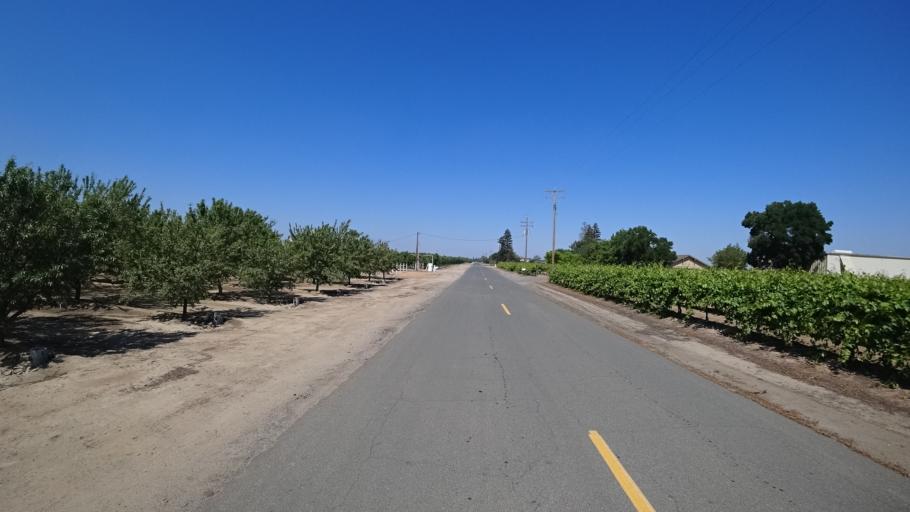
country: US
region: California
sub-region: Fresno County
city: Kingsburg
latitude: 36.4596
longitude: -119.5696
